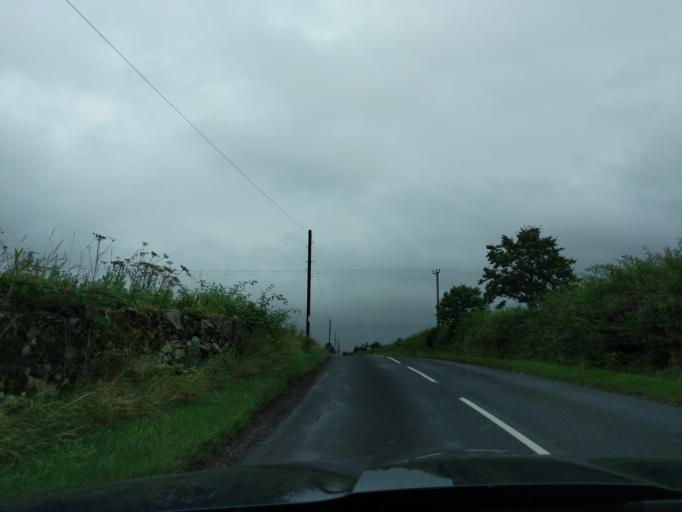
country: GB
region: England
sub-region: Northumberland
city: Ford
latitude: 55.6540
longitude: -2.1123
